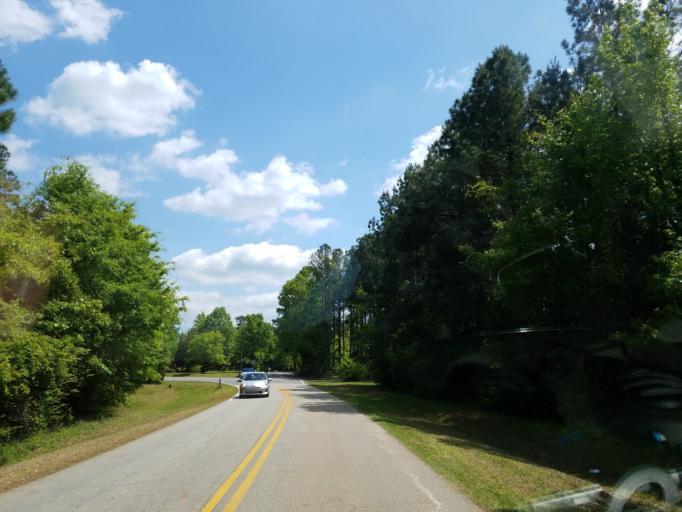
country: US
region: Georgia
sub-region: Monroe County
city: Forsyth
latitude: 33.0892
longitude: -83.9606
